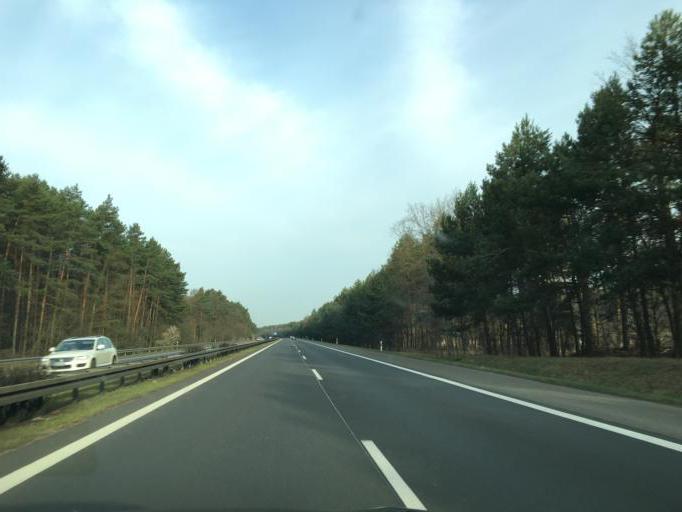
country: DE
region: Brandenburg
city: Birkenwerder
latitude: 52.6940
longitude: 13.3074
